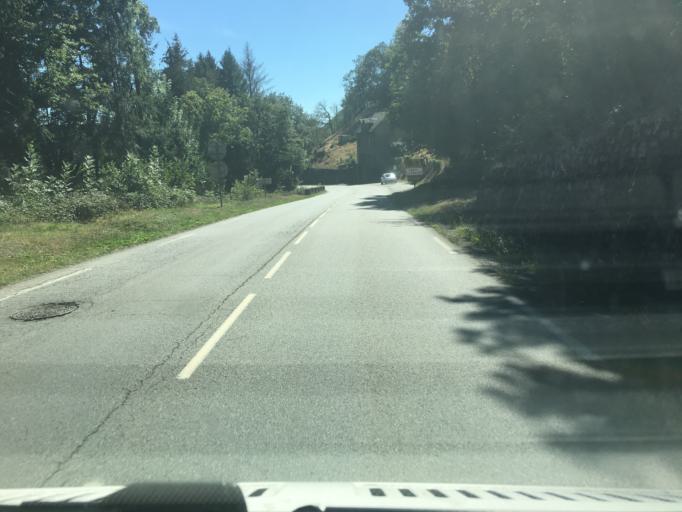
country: FR
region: Limousin
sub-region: Departement de la Correze
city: Bort-les-Orgues
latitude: 45.4056
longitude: 2.4973
